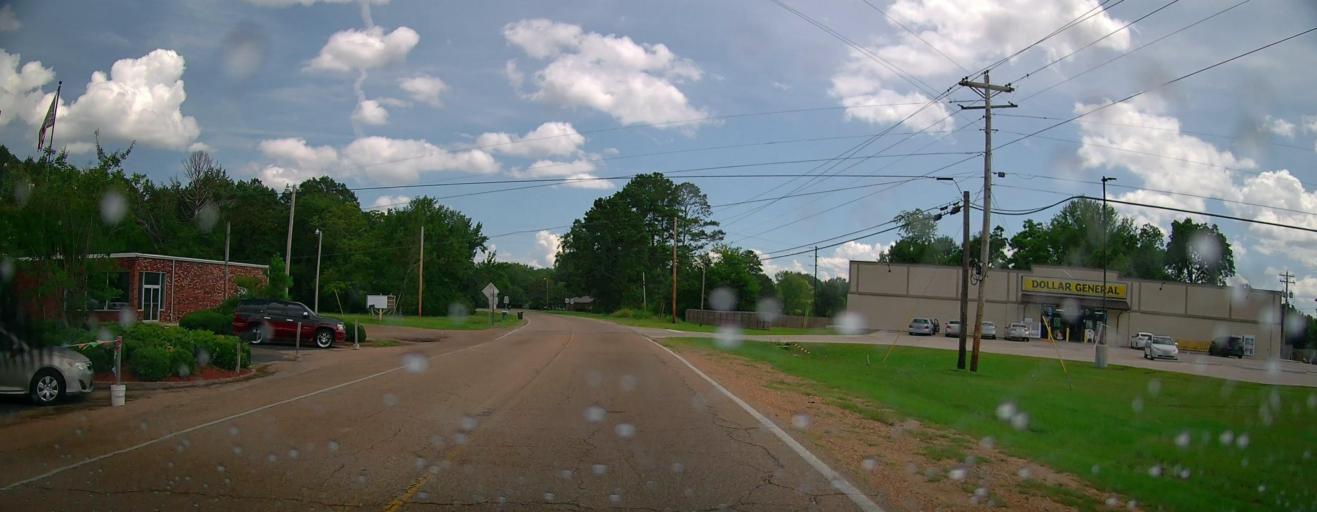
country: US
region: Mississippi
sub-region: Lee County
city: Shannon
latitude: 34.1253
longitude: -88.7187
